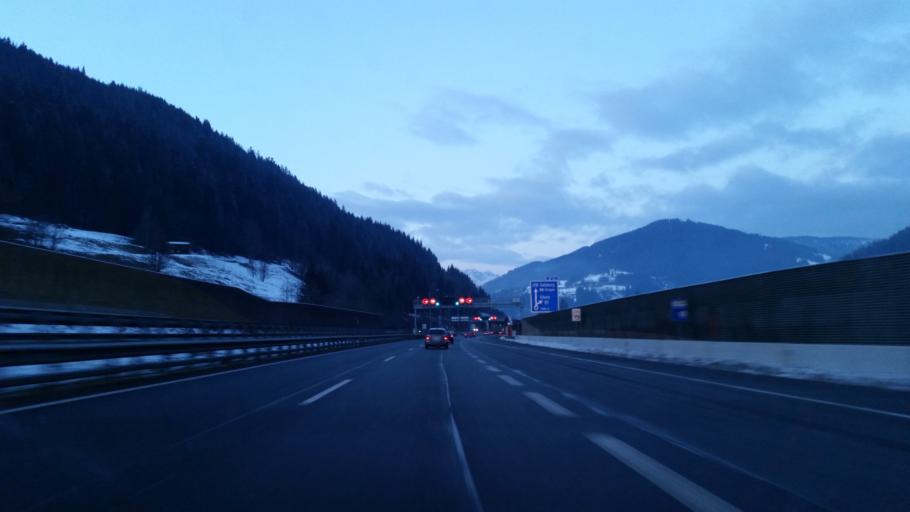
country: AT
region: Salzburg
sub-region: Politischer Bezirk Sankt Johann im Pongau
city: Eben im Pongau
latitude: 47.3967
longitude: 13.3959
